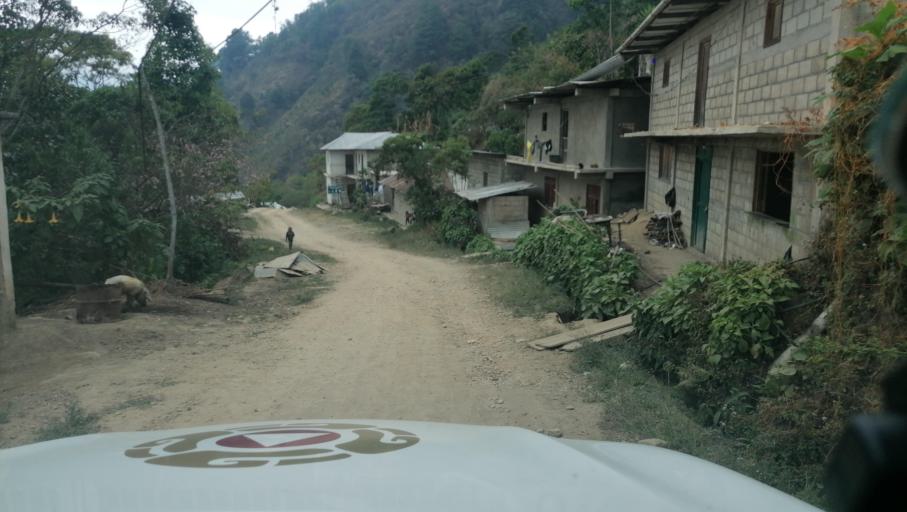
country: GT
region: San Marcos
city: Tacana
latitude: 15.2060
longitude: -92.1740
